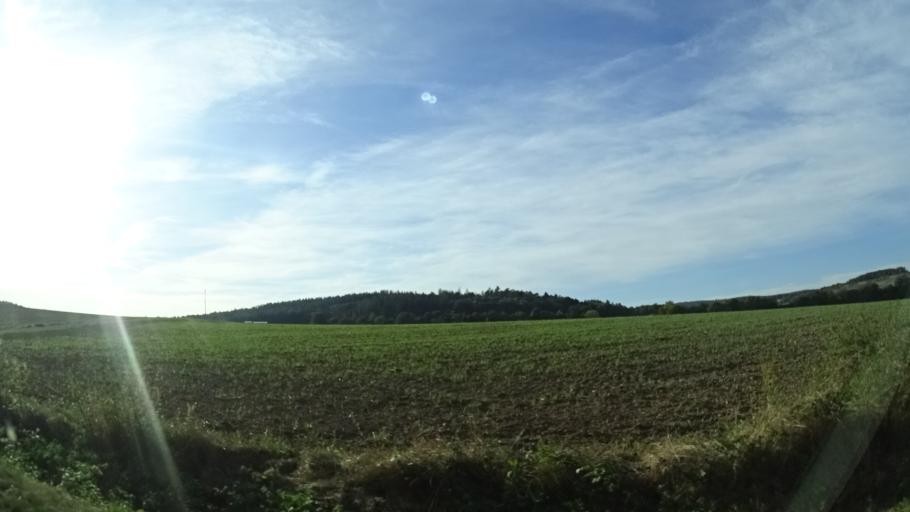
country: DE
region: Hesse
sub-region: Regierungsbezirk Kassel
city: Flieden
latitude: 50.4415
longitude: 9.5761
